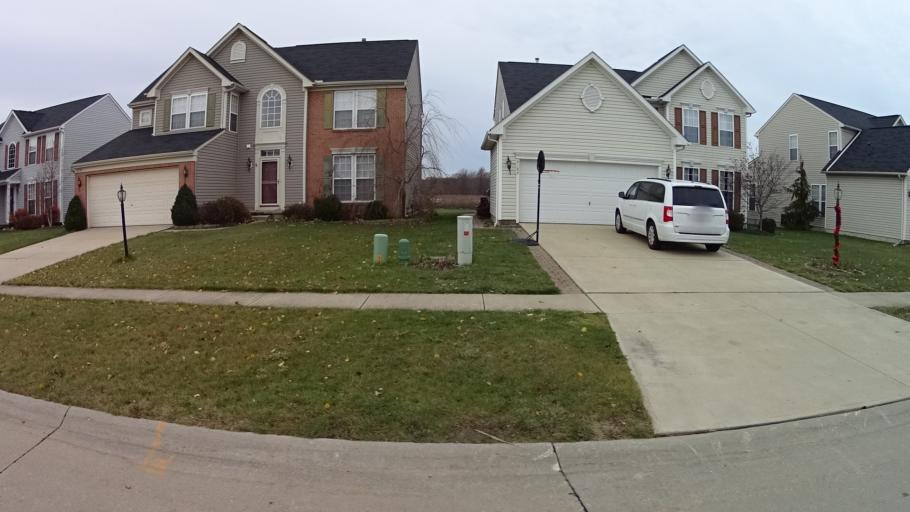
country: US
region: Ohio
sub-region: Lorain County
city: North Ridgeville
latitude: 41.4008
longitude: -82.0431
